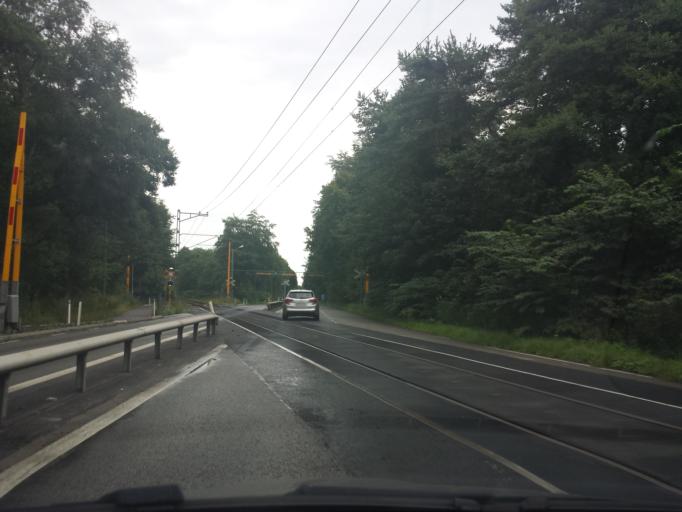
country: SE
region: Skane
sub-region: Ystads Kommun
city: Ystad
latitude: 55.4311
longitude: 13.8536
